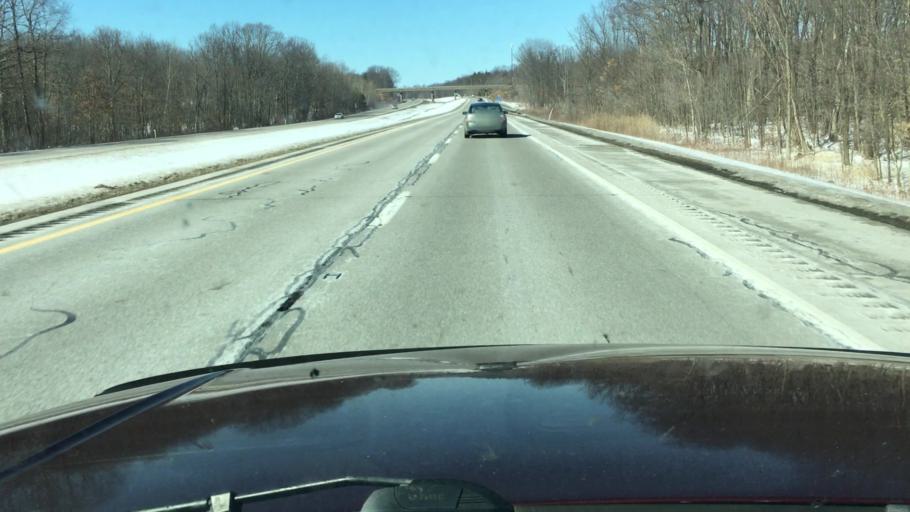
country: US
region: Pennsylvania
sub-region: Crawford County
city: Cochranton
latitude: 41.4866
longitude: -80.1664
